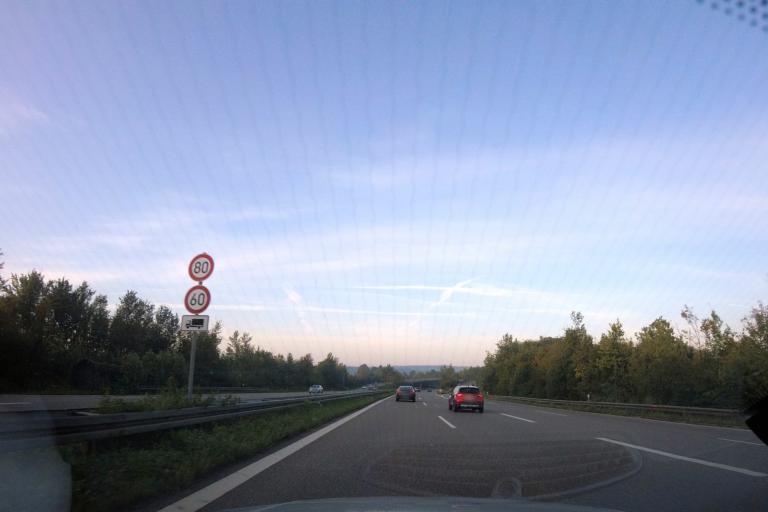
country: DE
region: Baden-Wuerttemberg
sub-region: Regierungsbezirk Stuttgart
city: Kornwestheim
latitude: 48.8422
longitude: 9.1764
